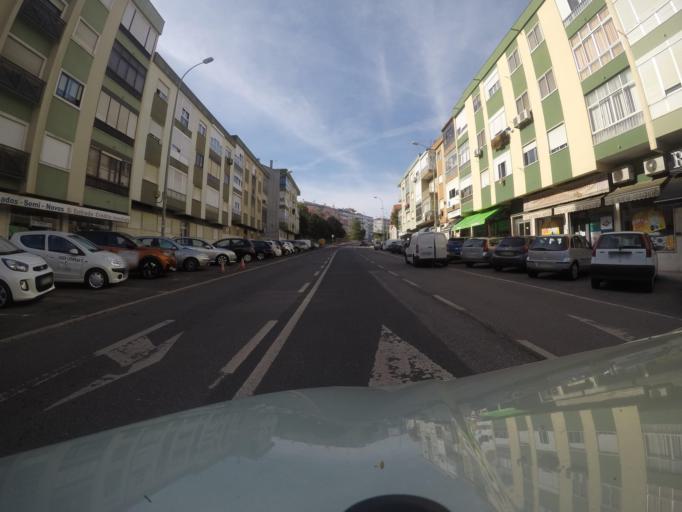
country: PT
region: Lisbon
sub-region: Amadora
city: Amadora
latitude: 38.7648
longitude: -9.2302
